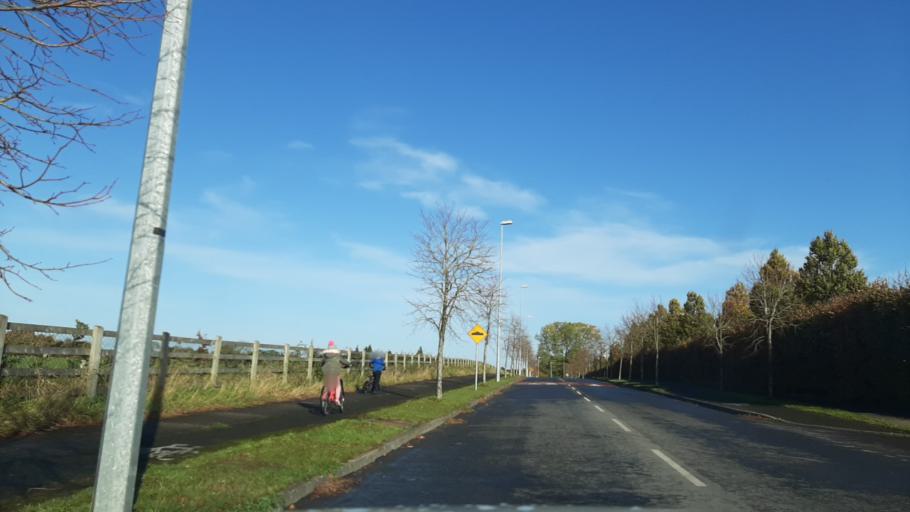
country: IE
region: Leinster
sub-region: Kildare
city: Rathangan
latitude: 53.2228
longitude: -7.0067
